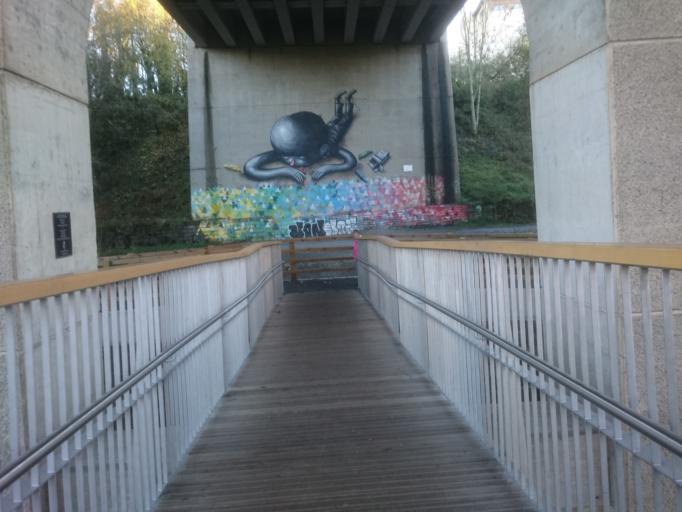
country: IE
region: Leinster
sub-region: Kilkenny
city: Kilkenny
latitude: 52.6437
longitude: -7.2306
